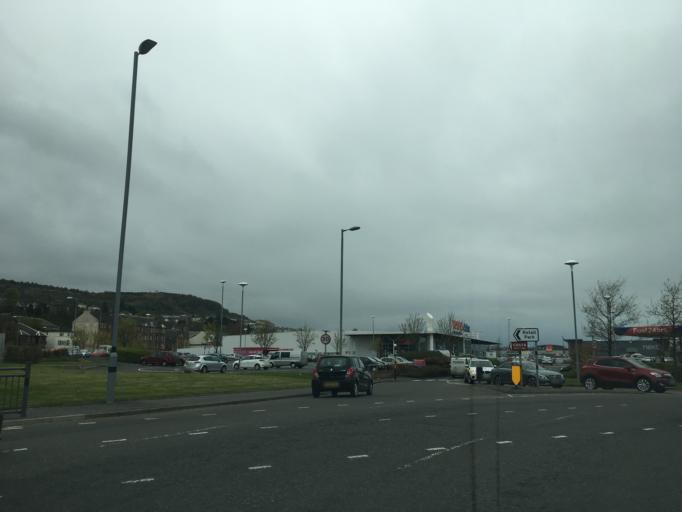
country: GB
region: Scotland
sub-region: Inverclyde
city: Port Glasgow
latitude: 55.9357
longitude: -4.6915
